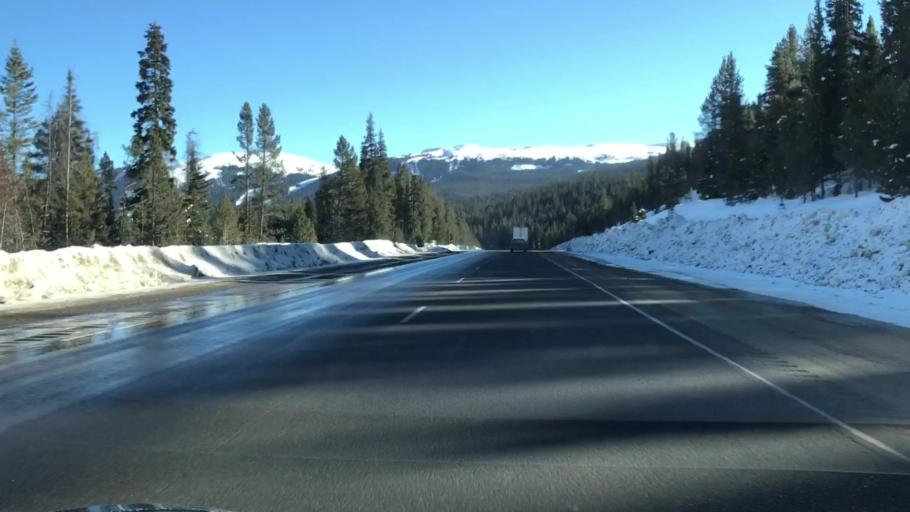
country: US
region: Colorado
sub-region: Summit County
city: Frisco
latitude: 39.5119
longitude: -106.2063
